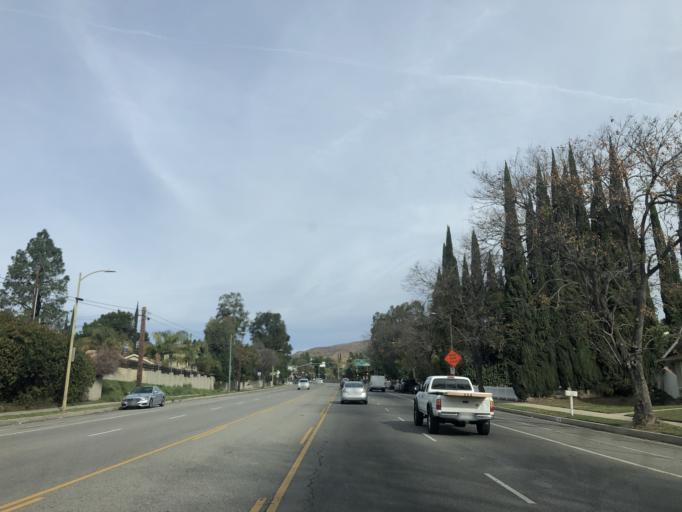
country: US
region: California
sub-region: Los Angeles County
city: Northridge
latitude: 34.2727
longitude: -118.5361
